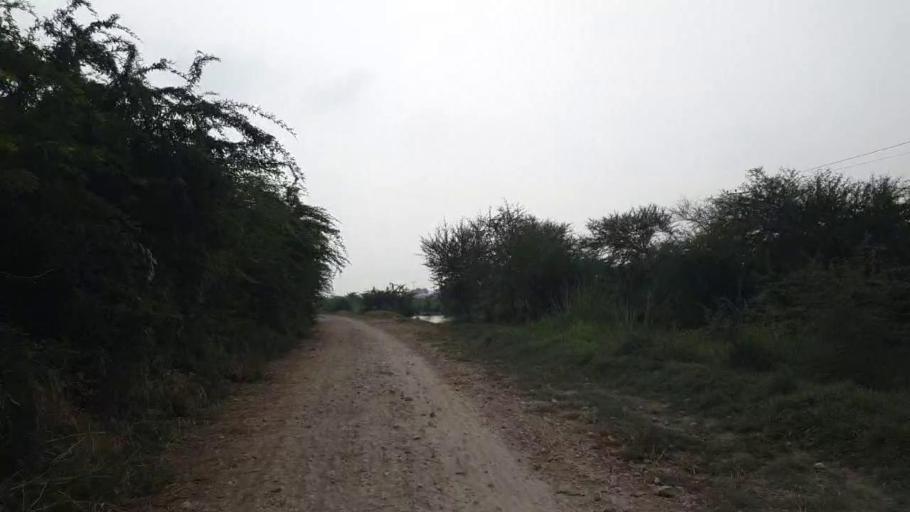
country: PK
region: Sindh
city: Kario
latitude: 24.8622
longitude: 68.5193
